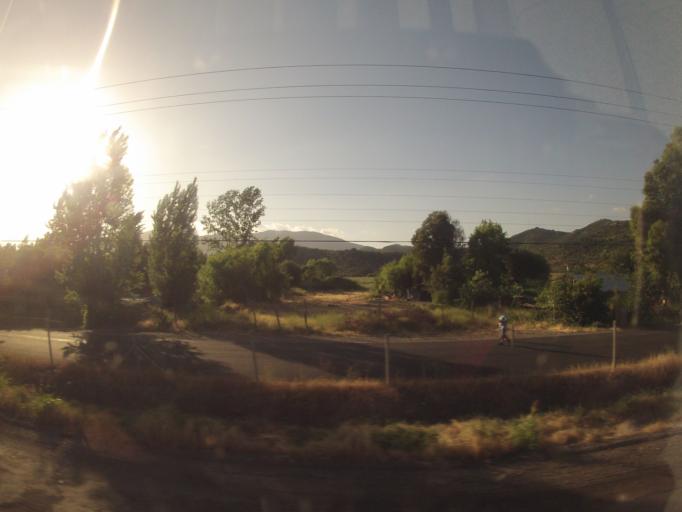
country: CL
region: O'Higgins
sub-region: Provincia de Cachapoal
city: Rengo
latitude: -34.5294
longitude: -70.9378
